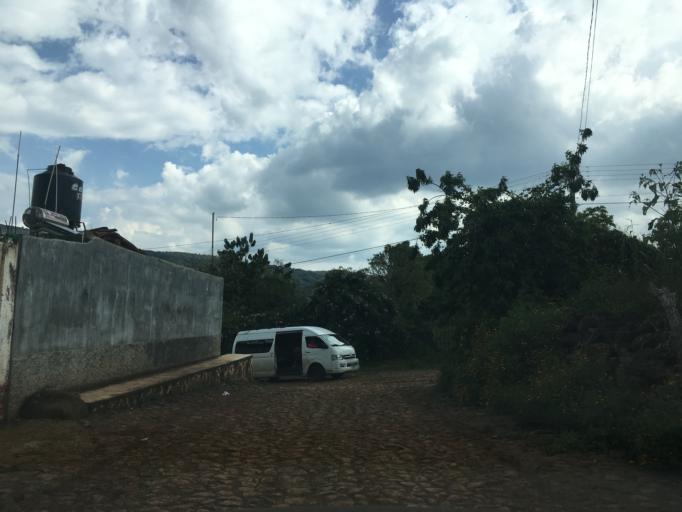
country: MX
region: Mexico
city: El Guayabito
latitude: 19.8985
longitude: -102.5000
